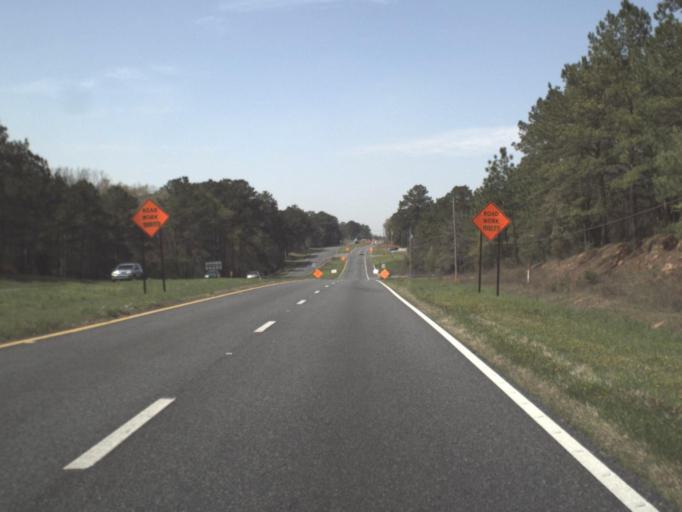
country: US
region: Florida
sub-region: Gadsden County
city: Quincy
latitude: 30.5631
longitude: -84.5398
